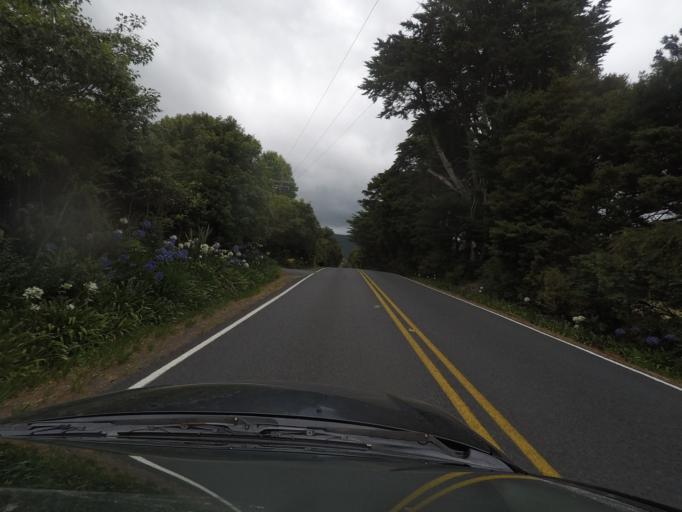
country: NZ
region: Auckland
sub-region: Auckland
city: Wellsford
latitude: -36.2867
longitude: 174.6312
